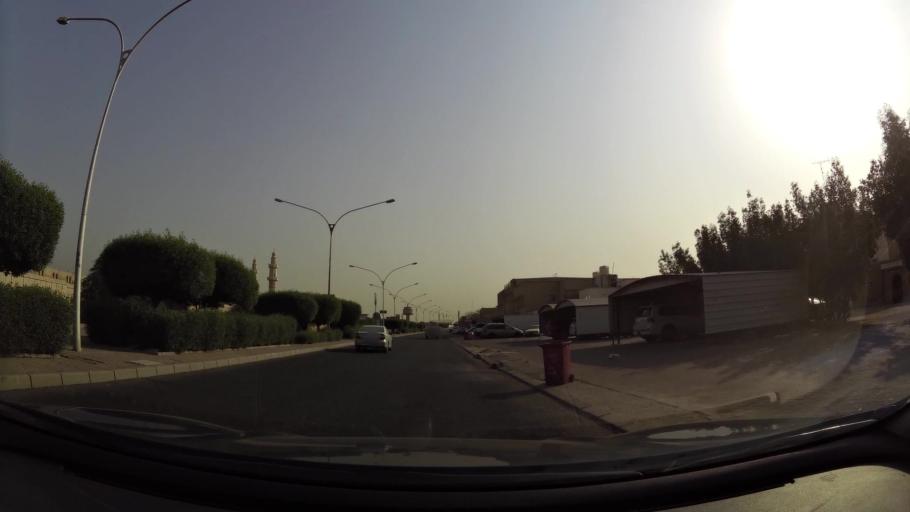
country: KW
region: Al Ahmadi
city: Al Manqaf
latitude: 29.1099
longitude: 48.1058
